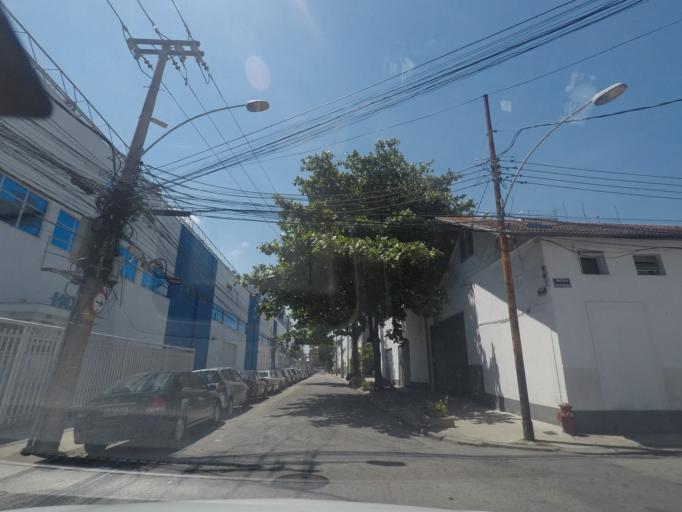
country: BR
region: Rio de Janeiro
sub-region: Rio De Janeiro
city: Rio de Janeiro
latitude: -22.9052
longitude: -43.2125
